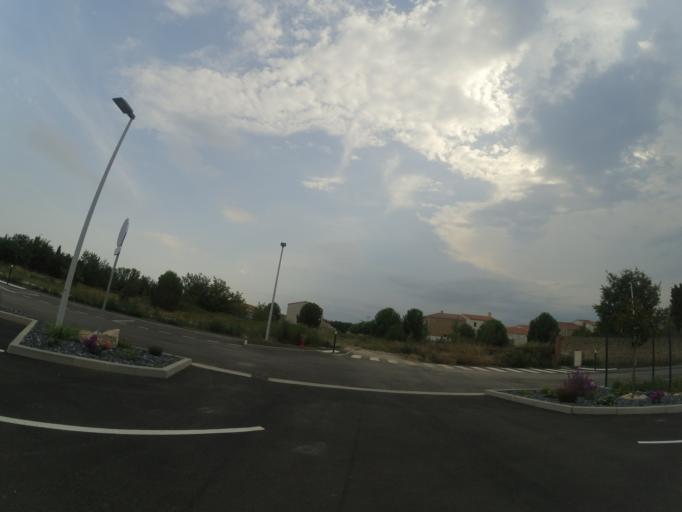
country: FR
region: Languedoc-Roussillon
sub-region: Departement des Pyrenees-Orientales
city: Corneilla-la-Riviere
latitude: 42.6841
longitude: 2.7246
